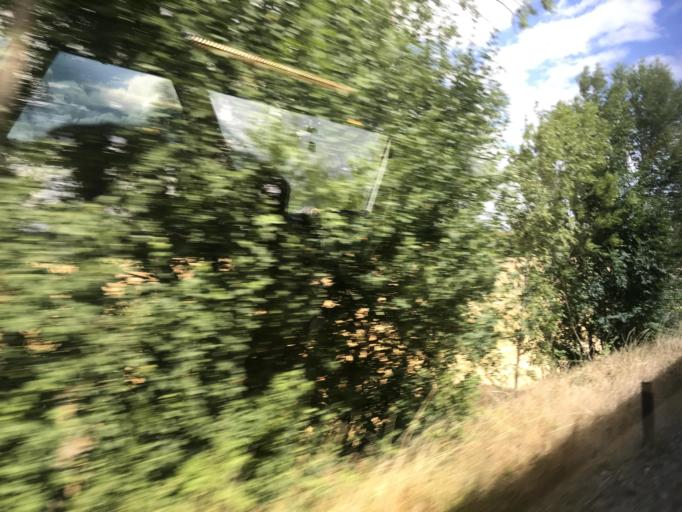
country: DE
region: Bavaria
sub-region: Regierungsbezirk Unterfranken
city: Elfershausen
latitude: 50.1437
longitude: 9.9922
